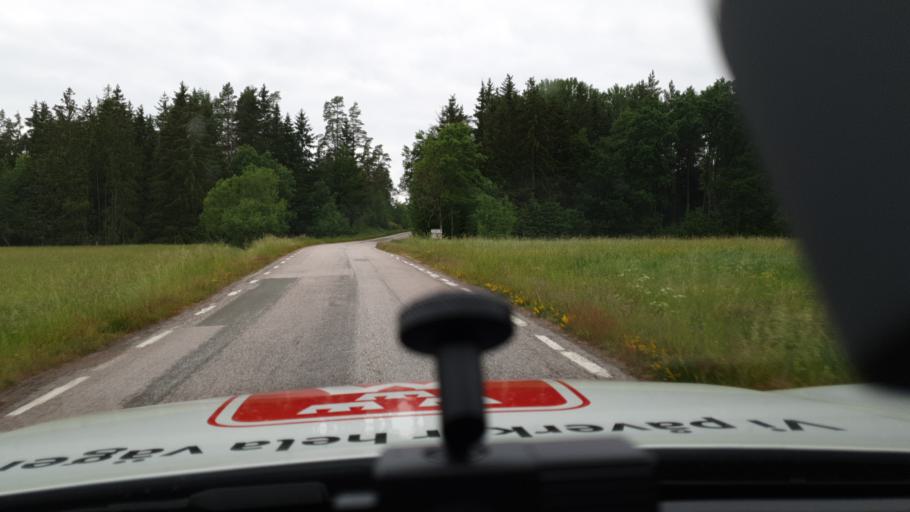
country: SE
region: Vaestra Goetaland
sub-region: Toreboda Kommun
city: Toereboda
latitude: 58.8272
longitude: 14.0030
